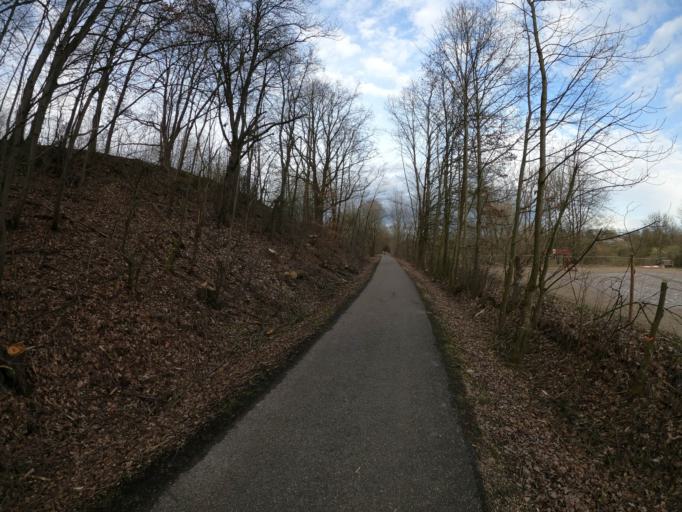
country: DE
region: Baden-Wuerttemberg
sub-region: Regierungsbezirk Stuttgart
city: Rechberghausen
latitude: 48.7213
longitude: 9.6390
